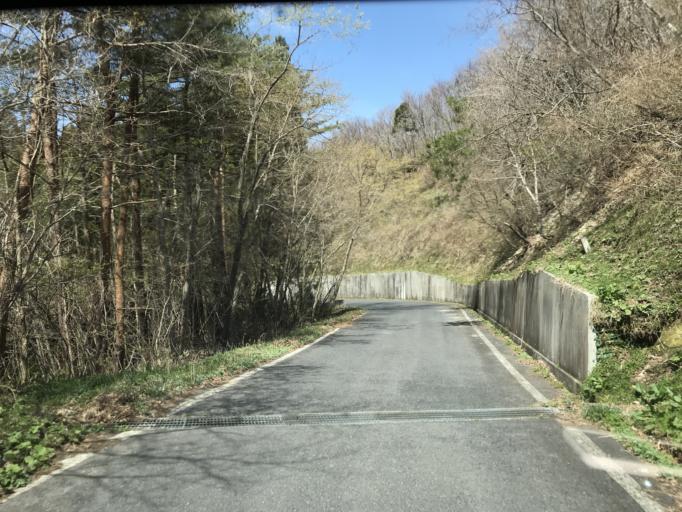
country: JP
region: Iwate
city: Ichinoseki
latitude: 38.8295
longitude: 141.2823
